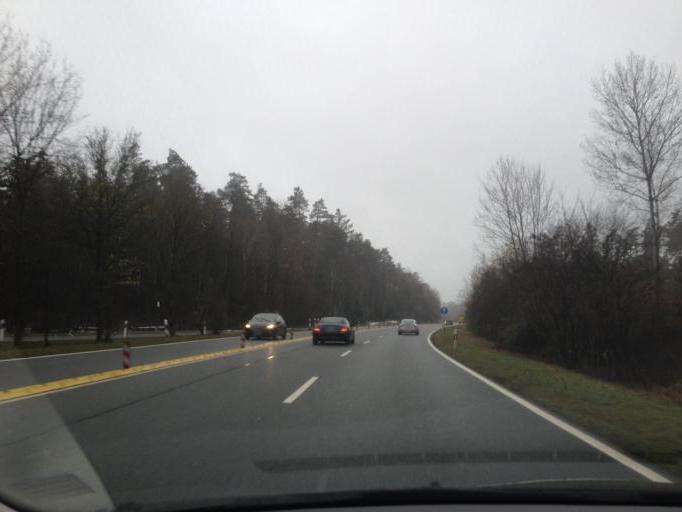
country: DE
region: Bavaria
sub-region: Regierungsbezirk Mittelfranken
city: Heroldsberg
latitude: 49.5167
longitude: 11.1445
